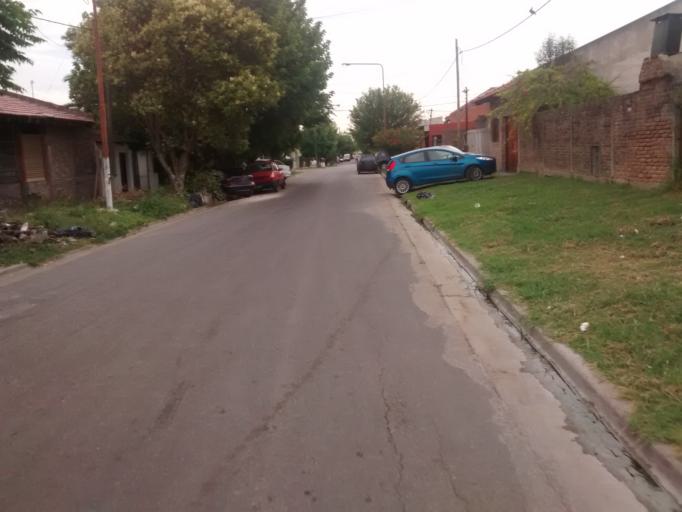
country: AR
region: Buenos Aires
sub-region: Partido de La Plata
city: La Plata
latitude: -34.9435
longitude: -57.9327
